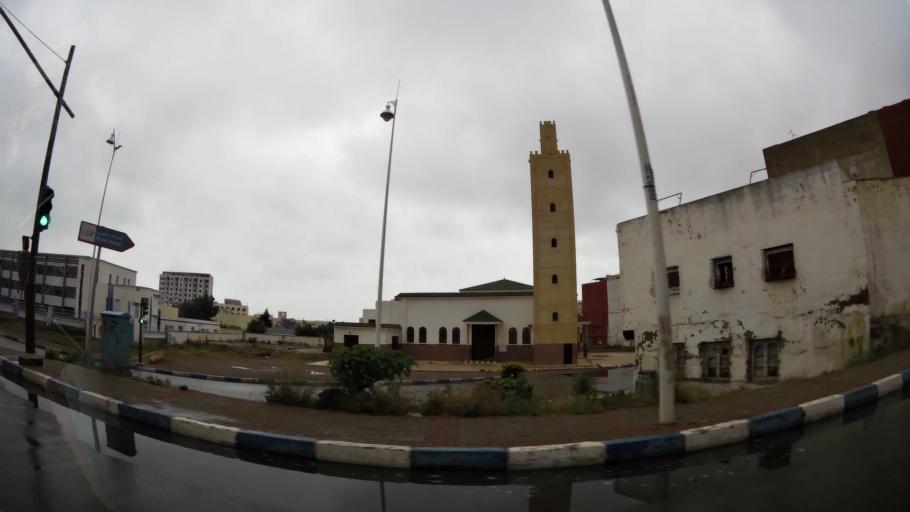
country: MA
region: Oriental
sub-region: Nador
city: Nador
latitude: 35.1827
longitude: -2.9279
